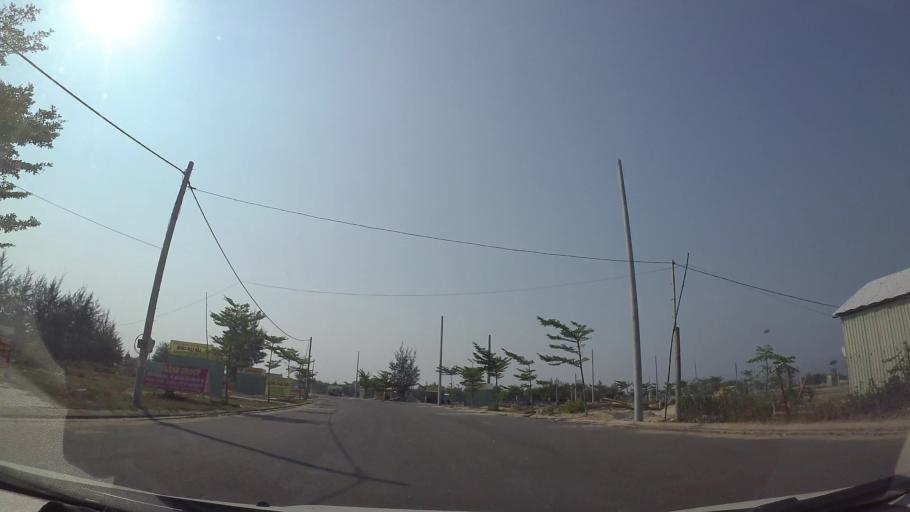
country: VN
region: Da Nang
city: Ngu Hanh Son
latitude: 15.9545
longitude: 108.2737
